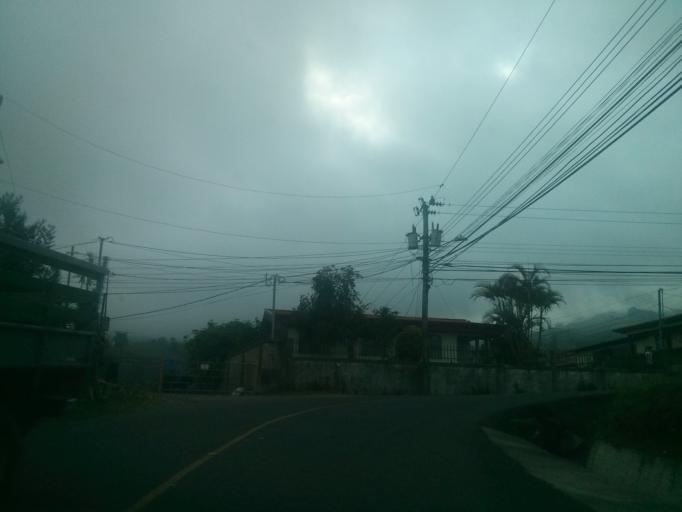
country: CR
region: Cartago
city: Cot
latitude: 9.9133
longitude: -83.8070
